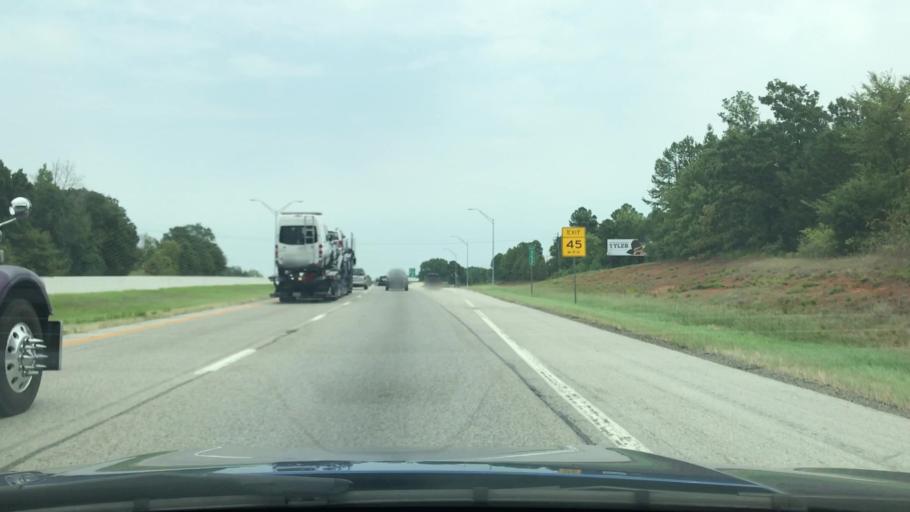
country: US
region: Texas
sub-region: Smith County
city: Hideaway
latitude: 32.4701
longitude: -95.4591
